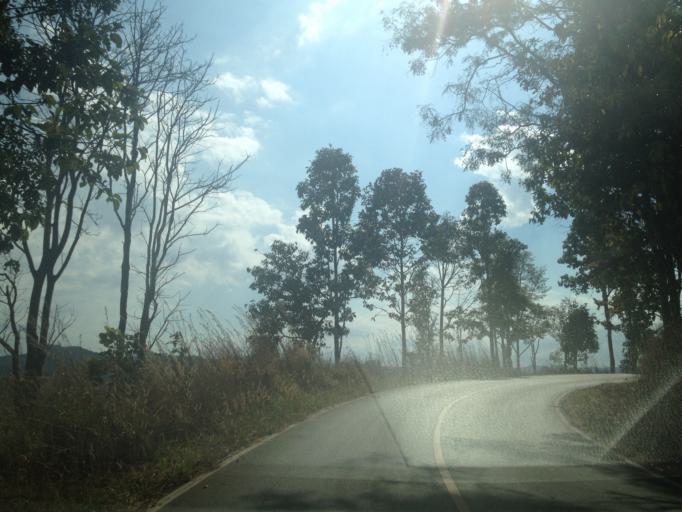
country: TH
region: Mae Hong Son
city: Ban Huai I Huak
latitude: 18.1173
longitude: 98.2183
